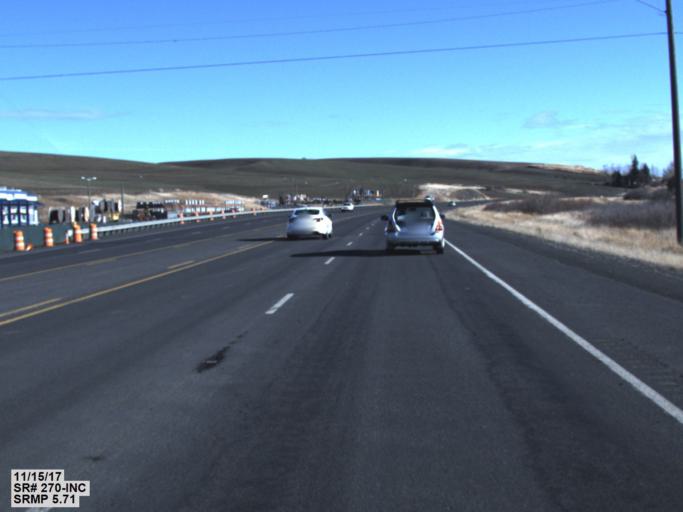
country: US
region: Washington
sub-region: Whitman County
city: Pullman
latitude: 46.7261
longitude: -117.1212
